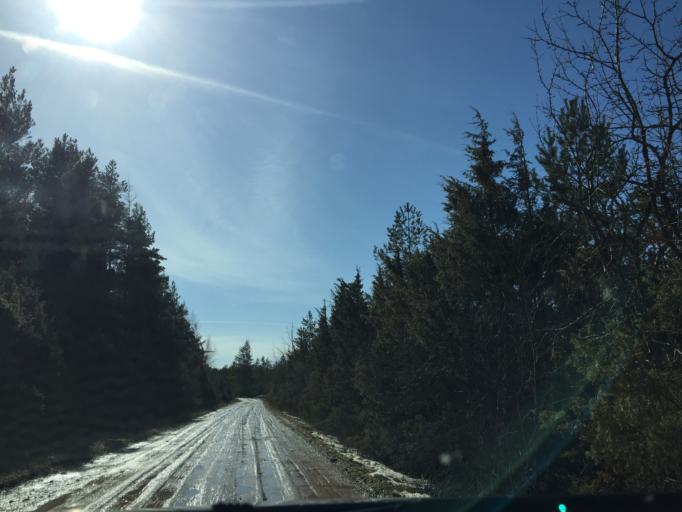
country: EE
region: Laeaene
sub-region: Haapsalu linn
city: Haapsalu
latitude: 58.6433
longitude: 23.5155
